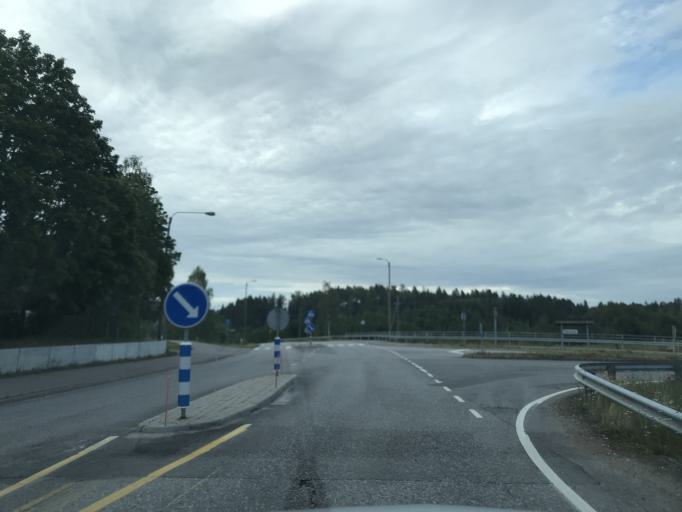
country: FI
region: Uusimaa
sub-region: Helsinki
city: Nurmijaervi
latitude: 60.3837
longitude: 24.6510
